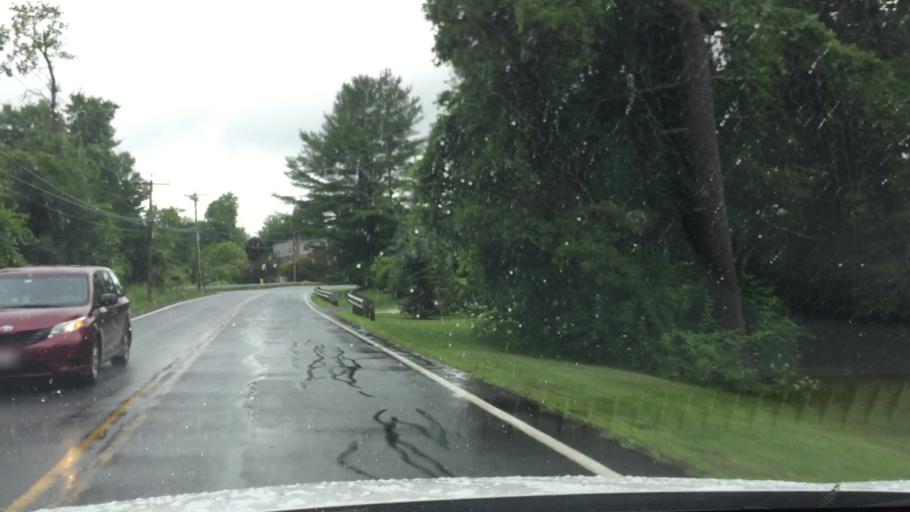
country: US
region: Massachusetts
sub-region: Berkshire County
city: Pittsfield
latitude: 42.4319
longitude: -73.2891
